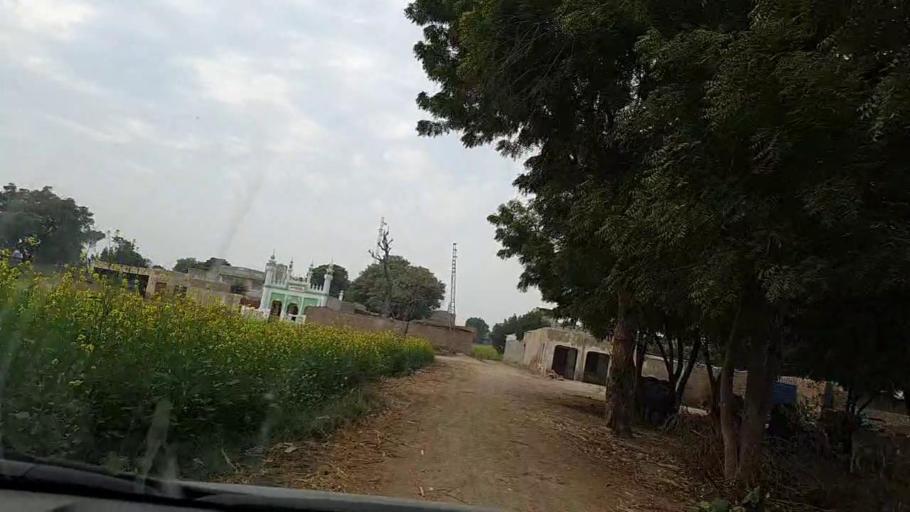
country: PK
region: Sindh
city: Daulatpur
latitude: 26.5633
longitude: 67.9780
